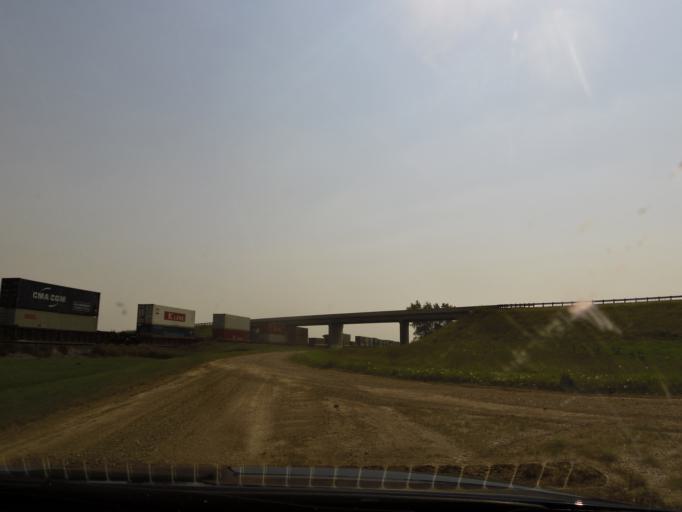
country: US
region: North Dakota
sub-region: Ransom County
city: Sheldon
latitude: 46.2611
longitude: -97.1216
